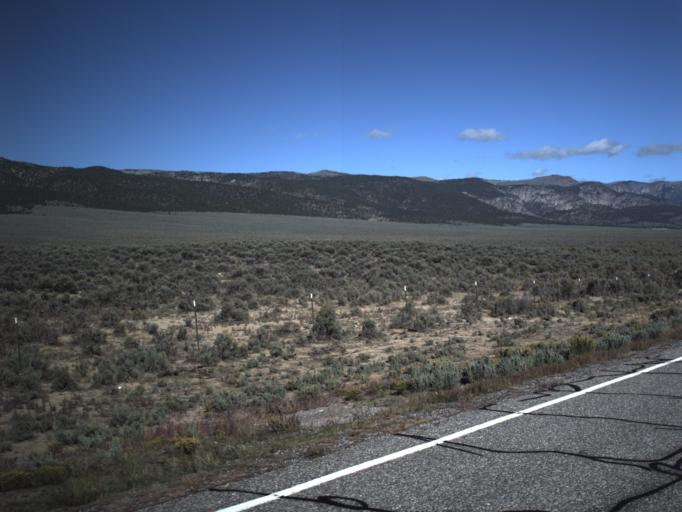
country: US
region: Utah
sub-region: Piute County
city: Junction
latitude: 38.2478
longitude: -111.9873
